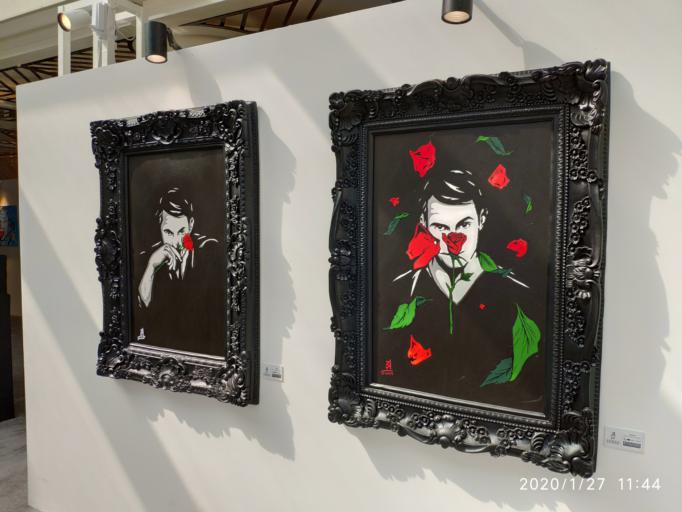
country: QA
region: Baladiyat ad Dawhah
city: Doha
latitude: 25.3615
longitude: 51.5239
